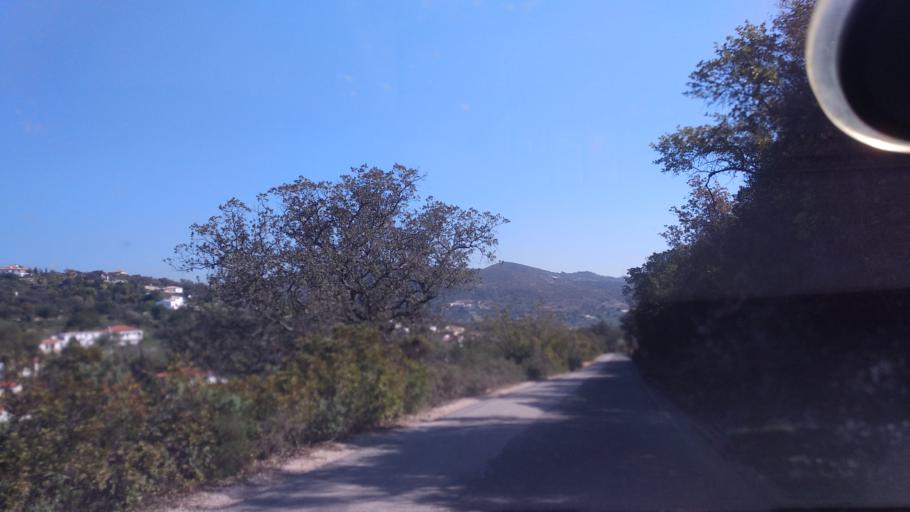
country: PT
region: Faro
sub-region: Faro
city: Santa Barbara de Nexe
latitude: 37.1118
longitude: -7.9209
